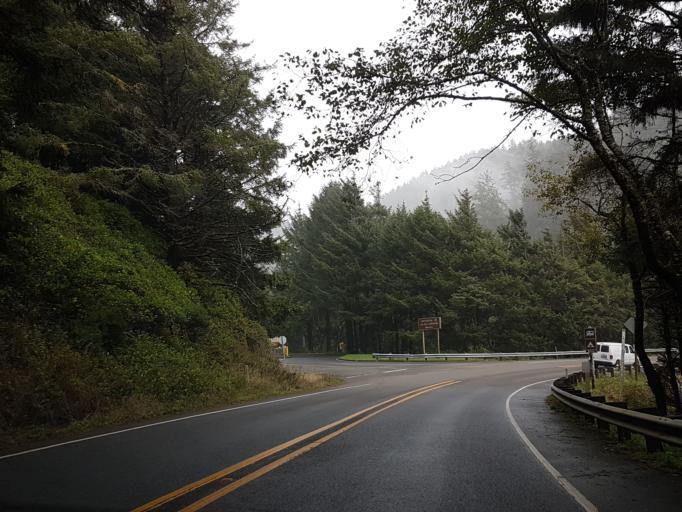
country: US
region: Oregon
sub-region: Lincoln County
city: Waldport
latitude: 44.2827
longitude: -124.1084
